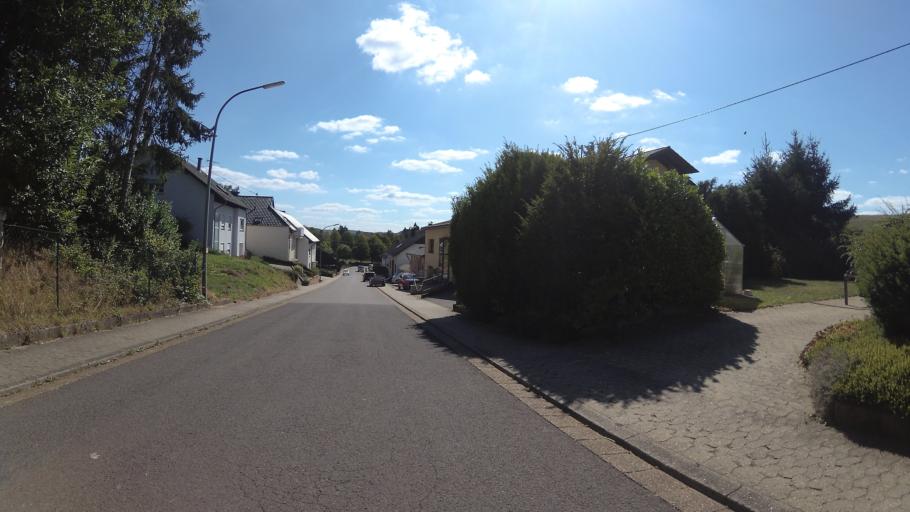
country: DE
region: Saarland
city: Lebach
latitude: 49.4286
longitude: 6.9168
